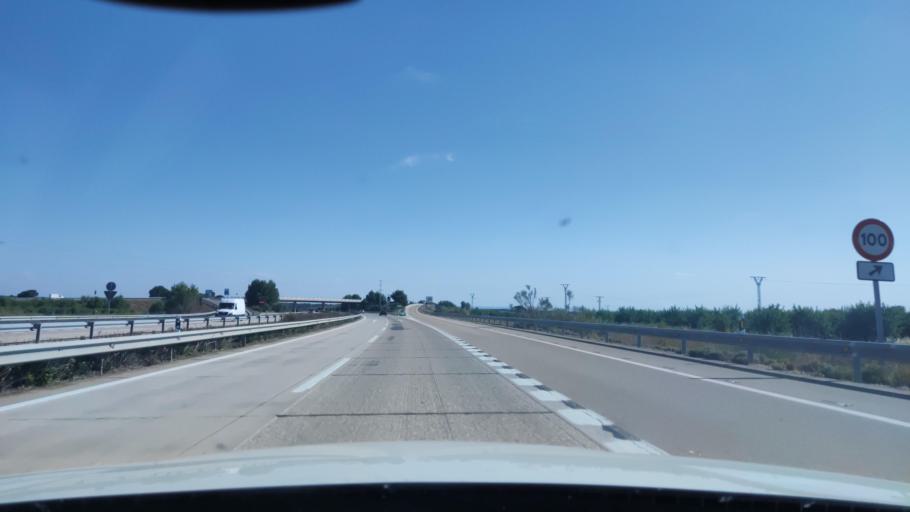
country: ES
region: Castille-La Mancha
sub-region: Provincia de Cuenca
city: Pozoamargo
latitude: 39.3630
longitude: -2.2040
